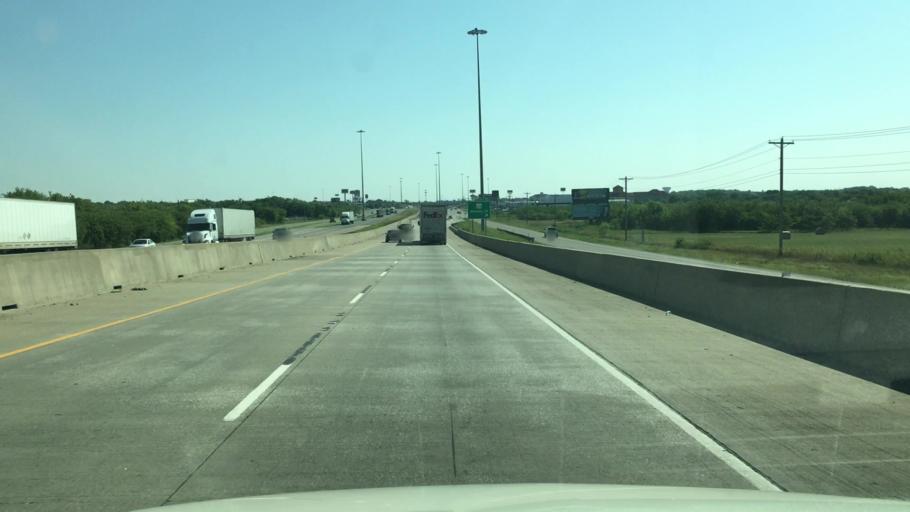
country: US
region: Texas
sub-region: Hunt County
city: Greenville
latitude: 33.0894
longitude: -96.1233
